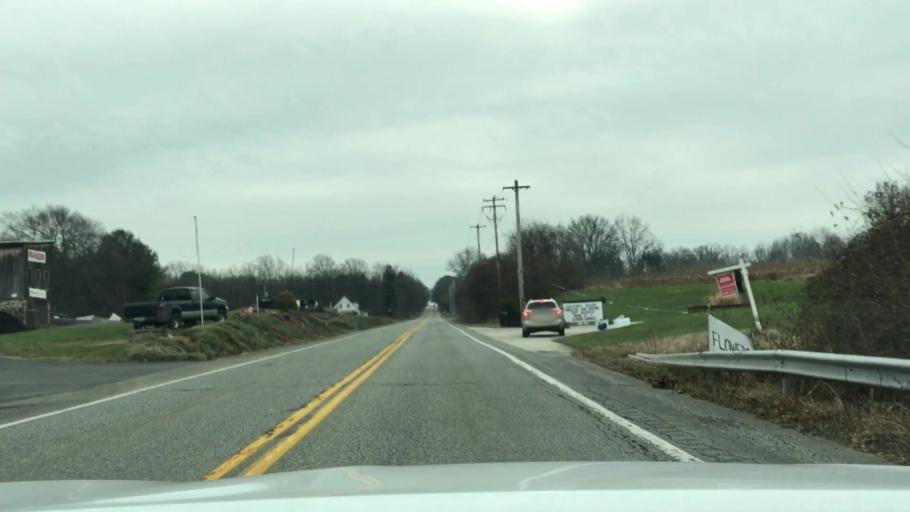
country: US
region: Pennsylvania
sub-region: Chester County
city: Spring City
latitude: 40.1941
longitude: -75.5788
